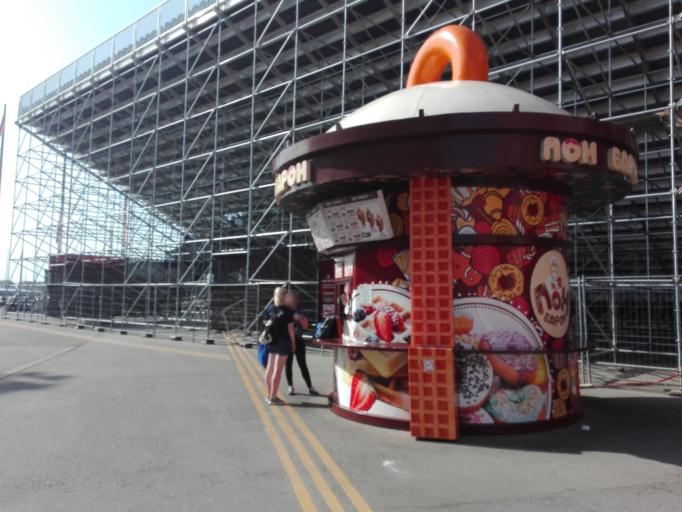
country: RU
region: Krasnodarskiy
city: Adler
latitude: 43.4055
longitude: 39.9577
